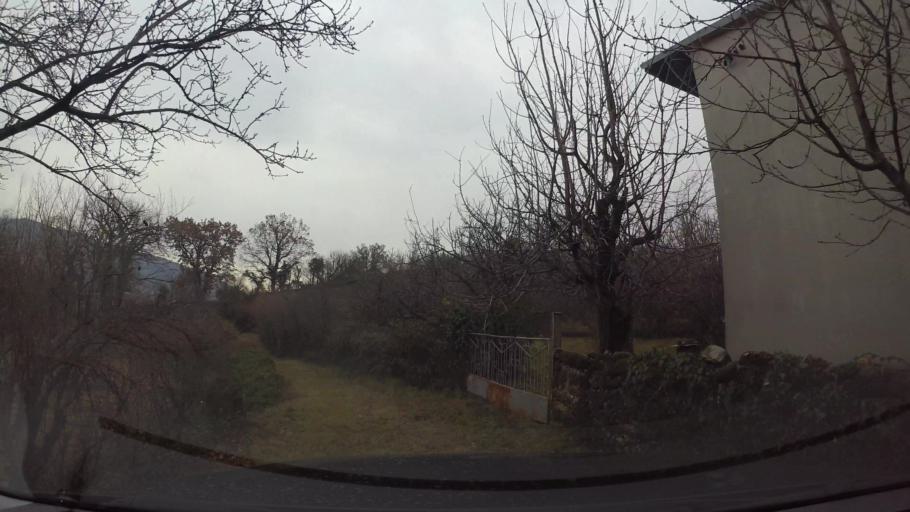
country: BA
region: Federation of Bosnia and Herzegovina
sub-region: Hercegovacko-Bosanski Kanton
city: Mostar
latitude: 43.3660
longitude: 17.8031
